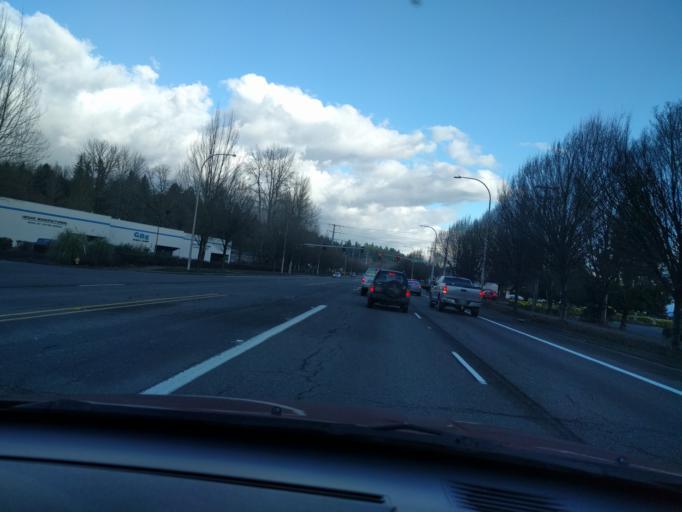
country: US
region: Oregon
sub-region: Clackamas County
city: Sunnyside
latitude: 45.4087
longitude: -122.5318
